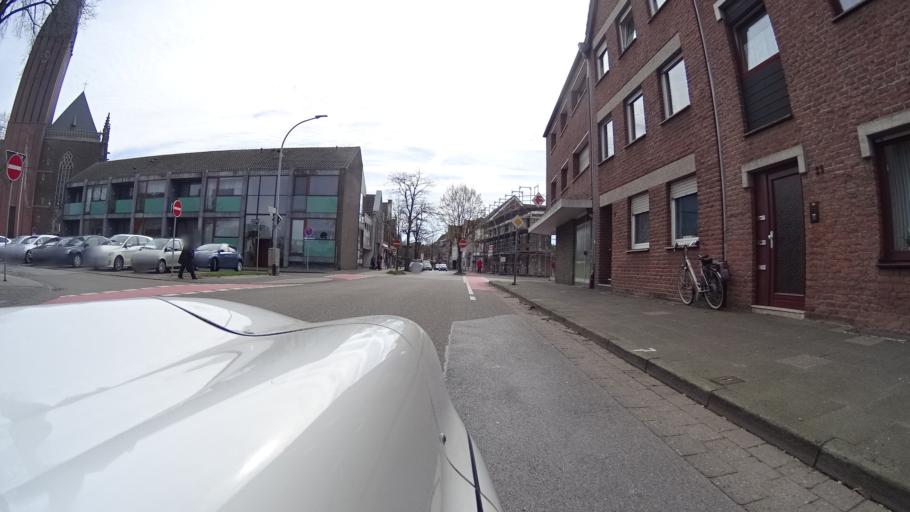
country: DE
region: North Rhine-Westphalia
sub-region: Regierungsbezirk Dusseldorf
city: Goch
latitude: 51.6770
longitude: 6.1539
